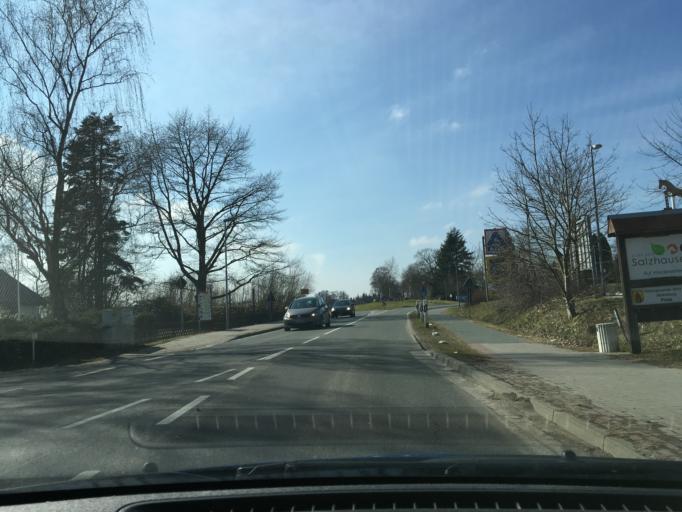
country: DE
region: Lower Saxony
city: Salzhausen
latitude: 53.2267
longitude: 10.1605
